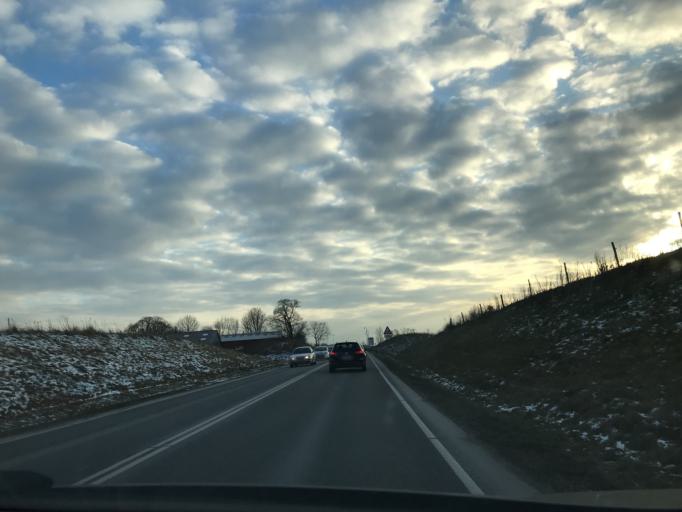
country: DK
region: Capital Region
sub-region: Egedal Kommune
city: Smorumnedre
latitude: 55.7216
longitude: 12.3148
